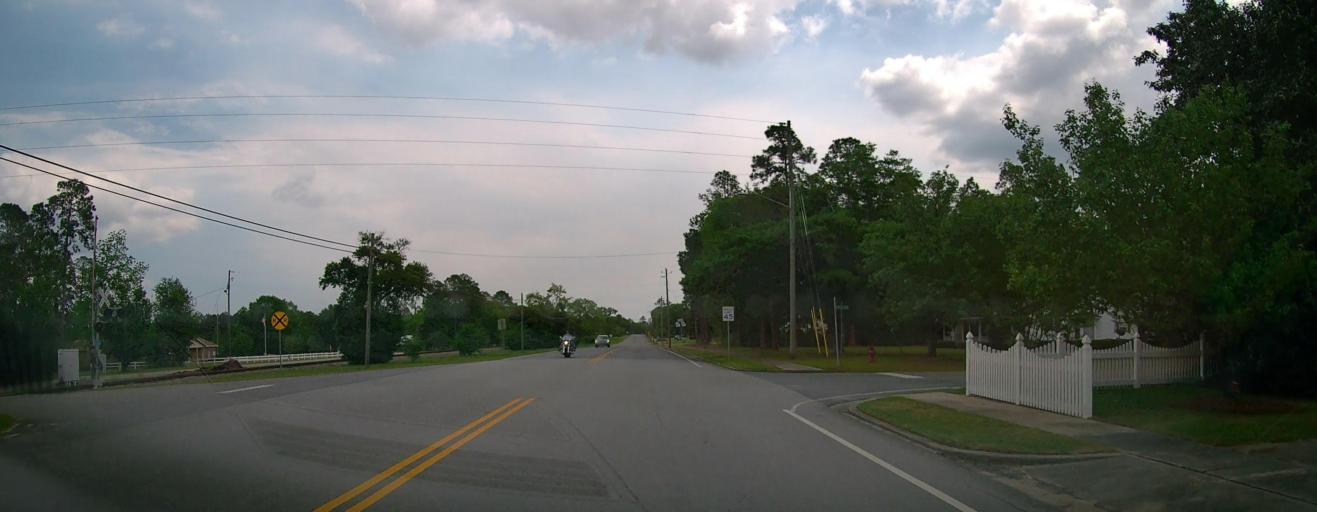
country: US
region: Georgia
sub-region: Treutlen County
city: Soperton
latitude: 32.3734
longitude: -82.5875
